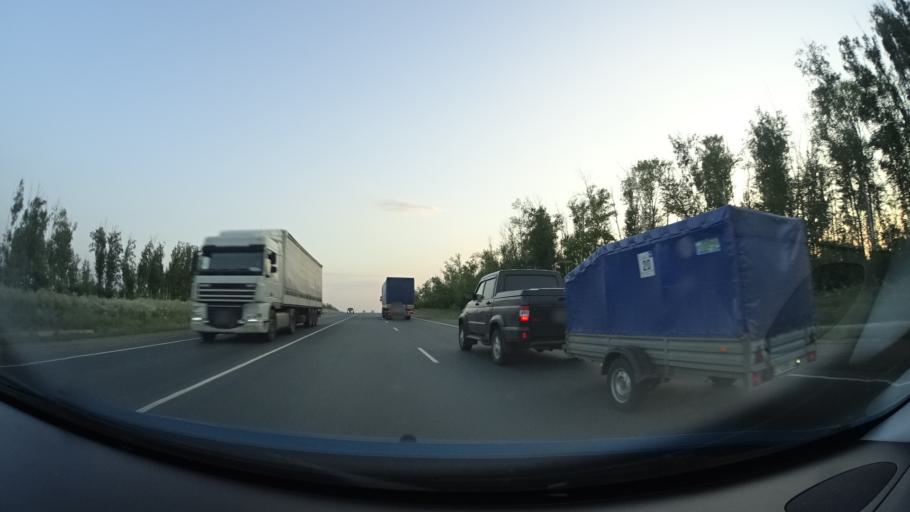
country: RU
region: Samara
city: Sukhodol
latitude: 53.8337
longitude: 51.0890
